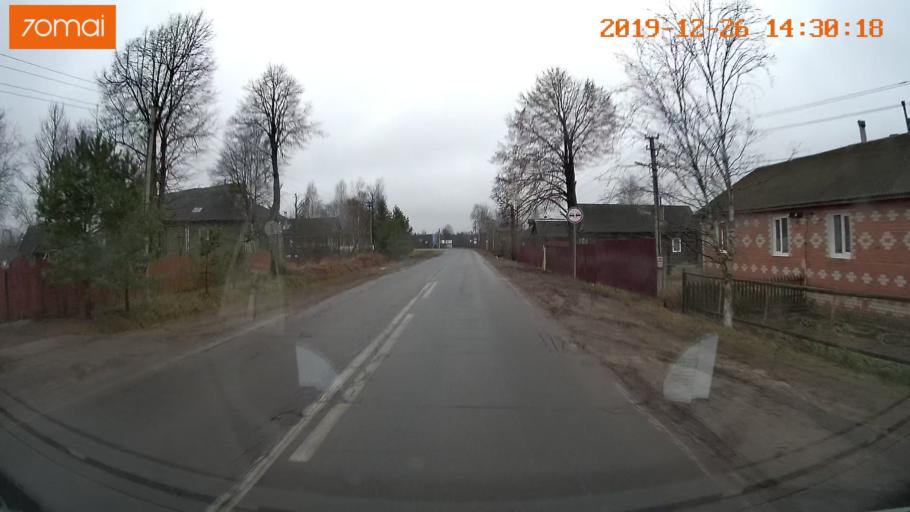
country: RU
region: Jaroslavl
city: Poshekhon'ye
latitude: 58.4552
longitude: 39.0368
